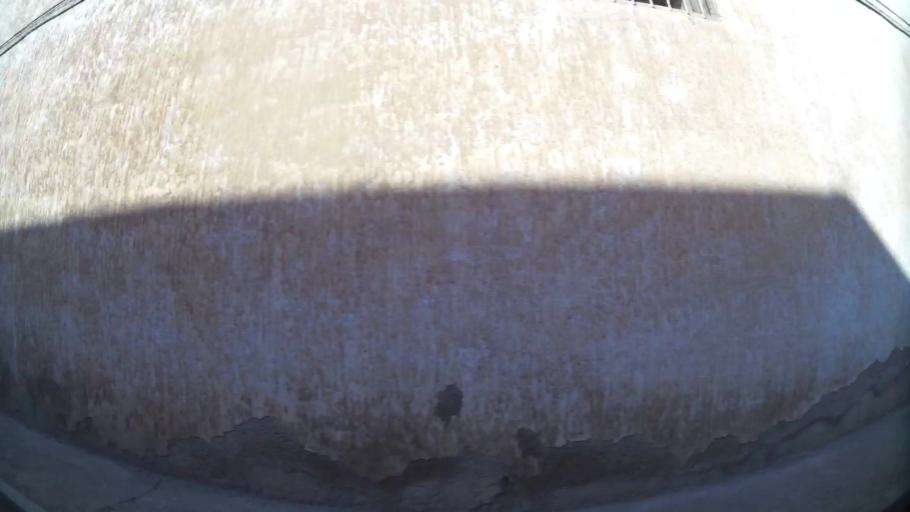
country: MA
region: Oriental
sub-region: Oujda-Angad
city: Oujda
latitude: 34.7100
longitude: -1.8902
